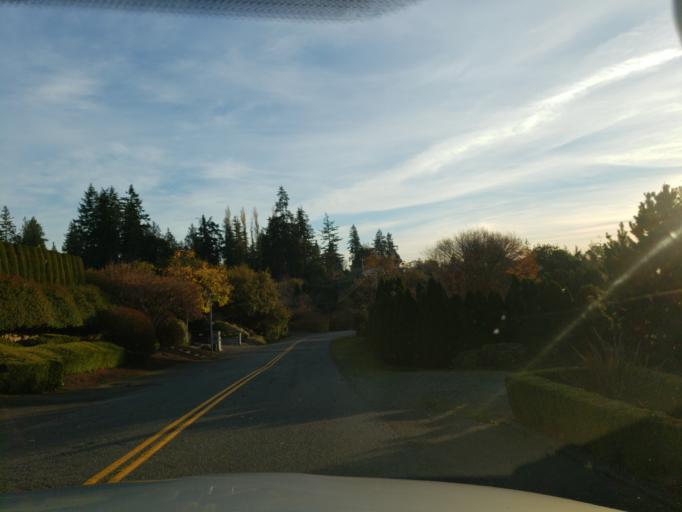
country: US
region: Washington
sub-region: King County
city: Shoreline
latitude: 47.7618
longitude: -122.3688
